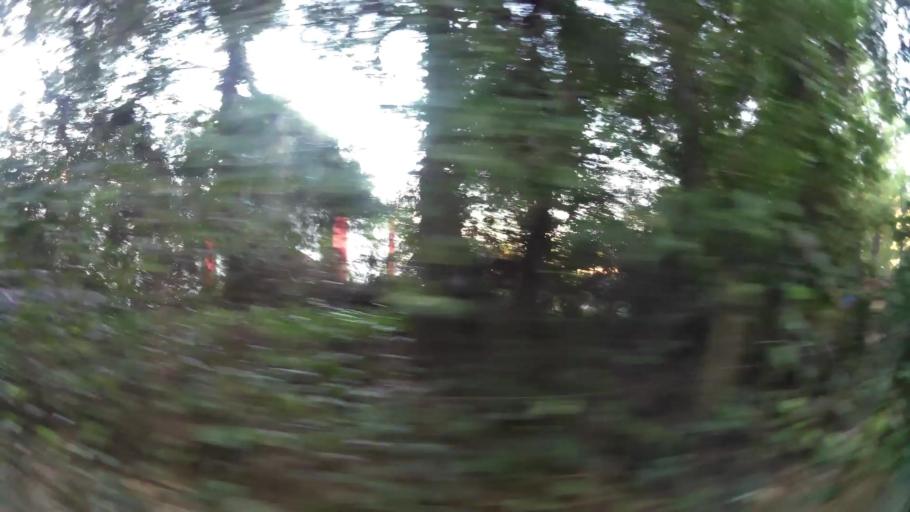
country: GR
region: Attica
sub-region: Nomarchia Anatolikis Attikis
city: Kryoneri
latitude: 38.1355
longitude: 23.8397
